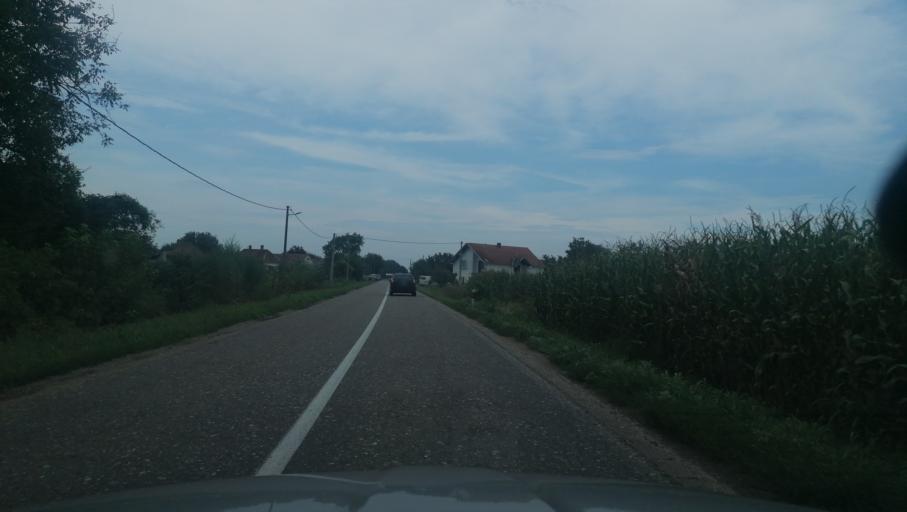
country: RS
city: Klenje
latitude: 44.8193
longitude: 19.4501
